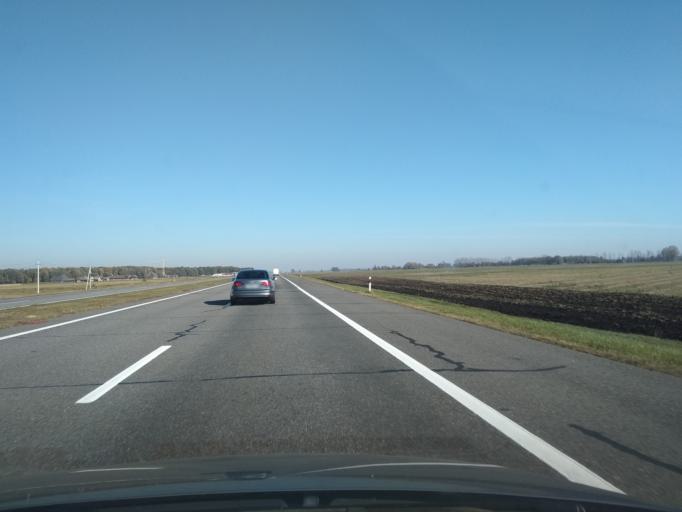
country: BY
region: Brest
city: Antopal'
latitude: 52.4065
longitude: 24.8020
